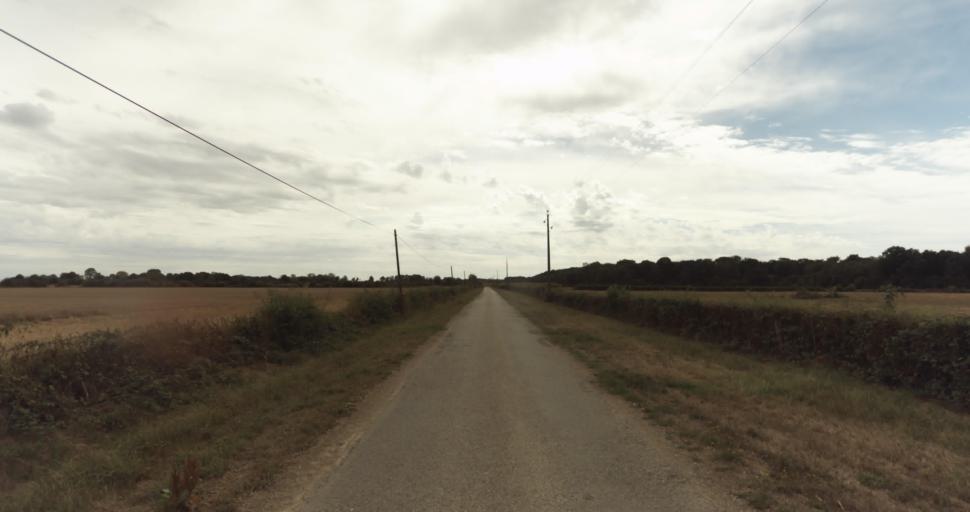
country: FR
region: Lower Normandy
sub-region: Departement du Calvados
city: La Vespiere
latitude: 48.9390
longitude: 0.3283
